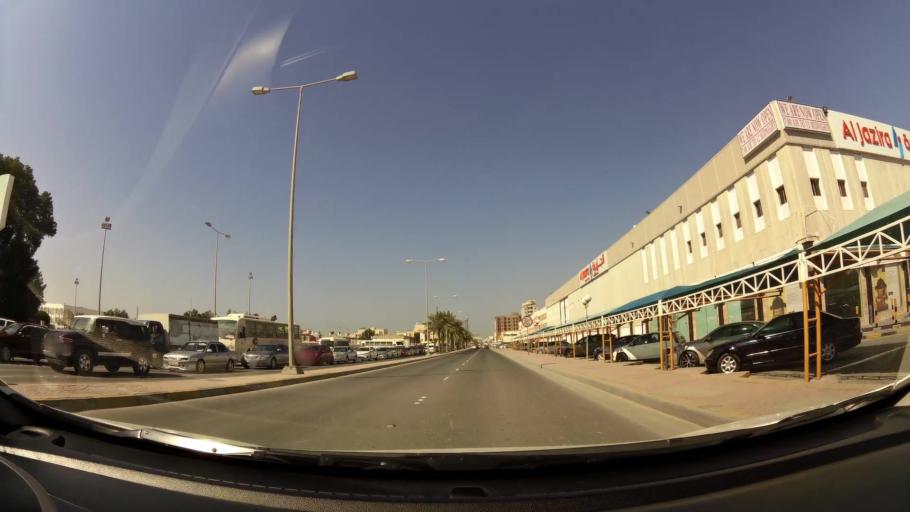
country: BH
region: Manama
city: Manama
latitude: 26.2068
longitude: 50.5756
